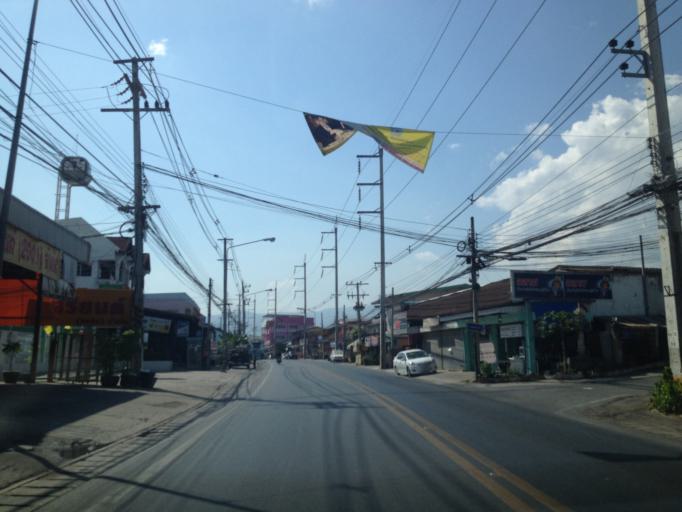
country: TH
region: Chiang Mai
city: Chom Thong
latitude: 18.4289
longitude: 98.6818
